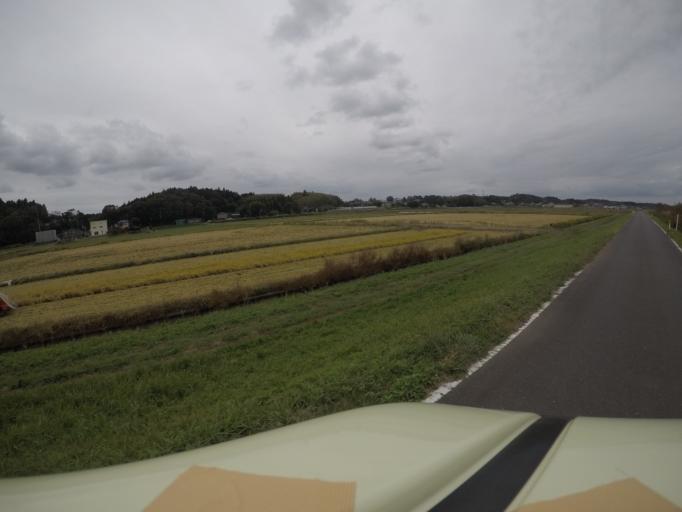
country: JP
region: Ibaraki
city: Ami
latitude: 36.0339
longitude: 140.2624
